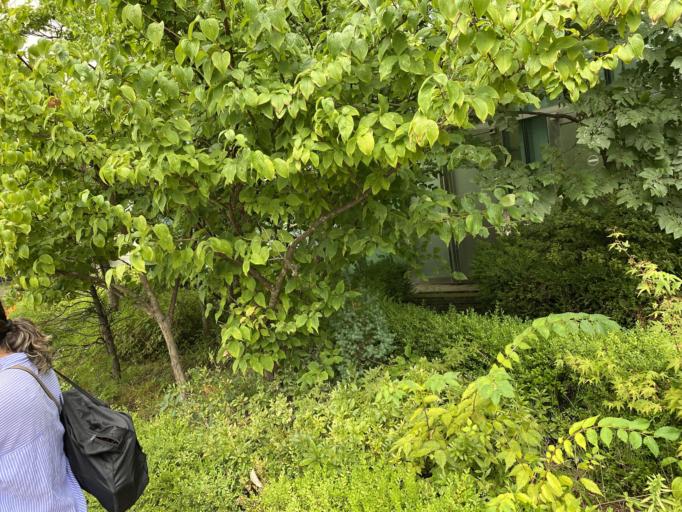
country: KR
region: Incheon
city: Incheon
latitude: 37.4927
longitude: 126.4902
